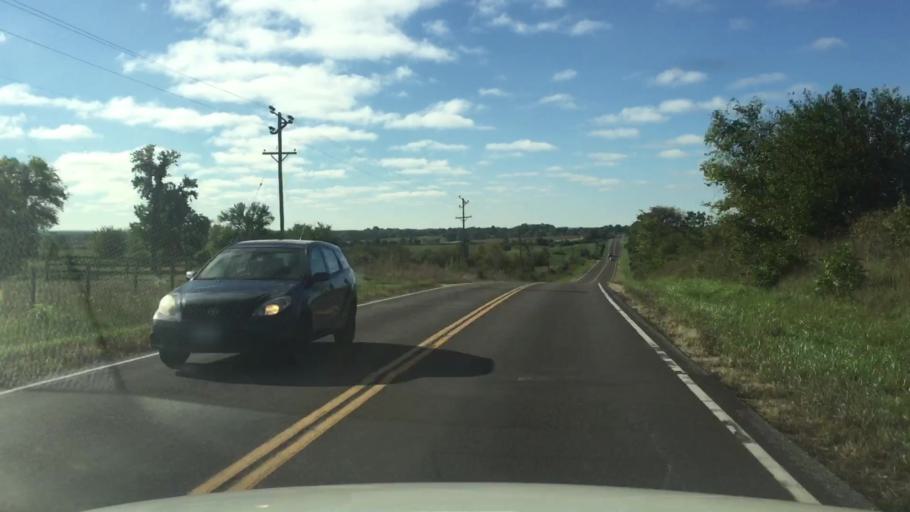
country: US
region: Missouri
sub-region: Howard County
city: New Franklin
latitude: 39.0831
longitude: -92.7455
